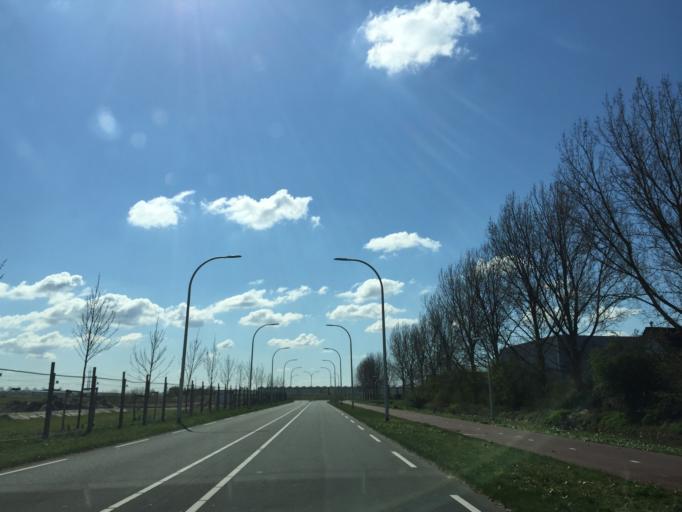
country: NL
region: South Holland
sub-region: Gemeente Pijnacker-Nootdorp
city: Pijnacker
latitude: 52.0291
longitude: 4.4443
